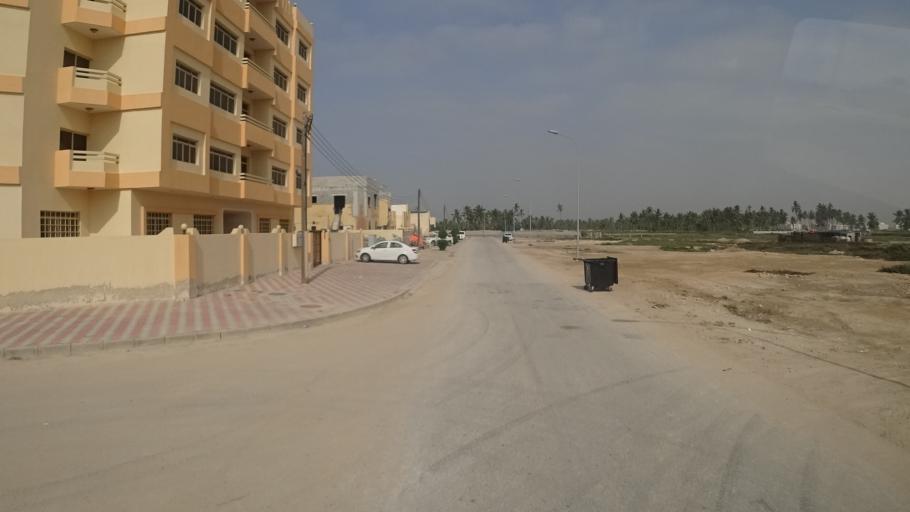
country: OM
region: Zufar
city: Salalah
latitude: 17.0160
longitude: 54.1723
